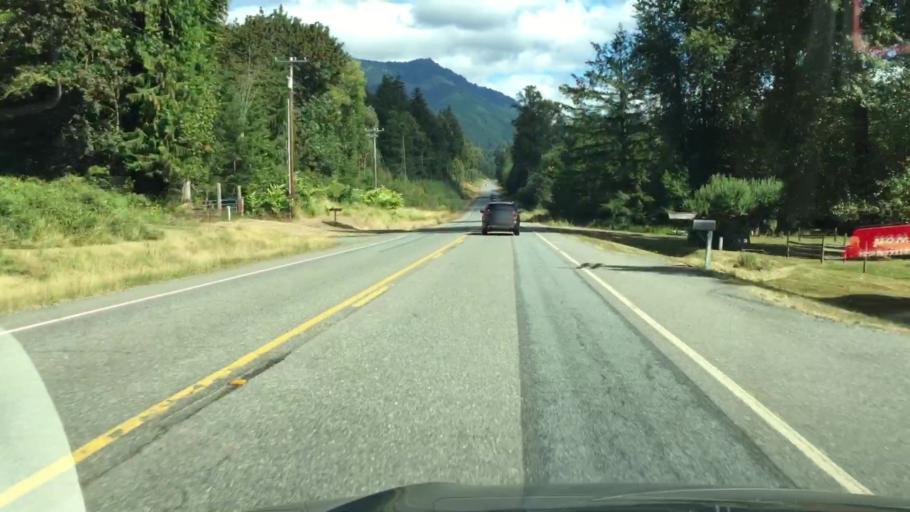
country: US
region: Washington
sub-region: Pierce County
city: Eatonville
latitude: 46.7570
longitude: -122.0029
